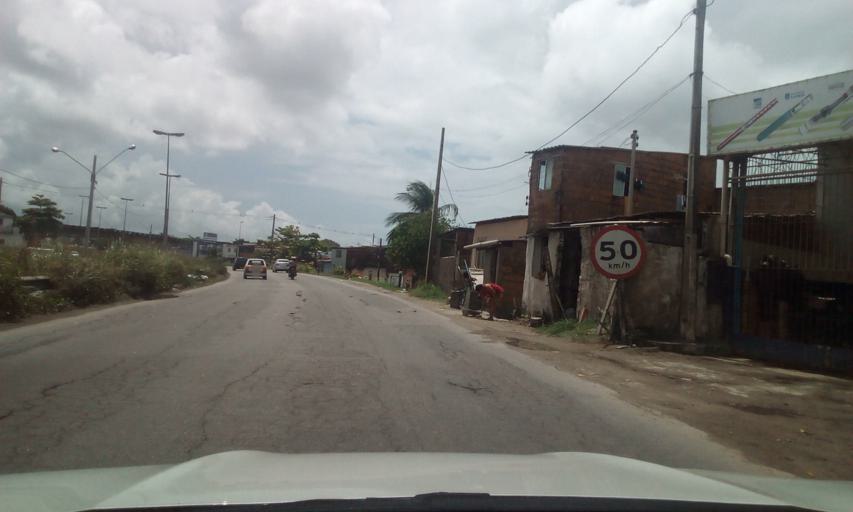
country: BR
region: Pernambuco
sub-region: Recife
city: Recife
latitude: -8.0833
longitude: -34.9437
